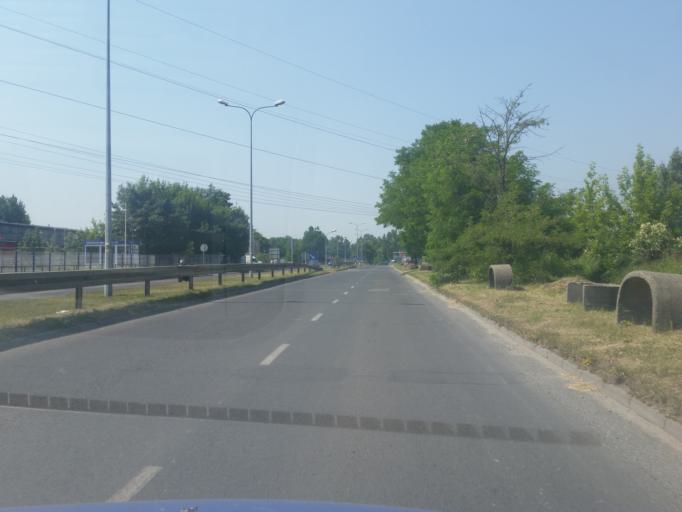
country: PL
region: Silesian Voivodeship
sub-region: Sosnowiec
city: Sosnowiec
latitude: 50.2556
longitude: 19.1311
